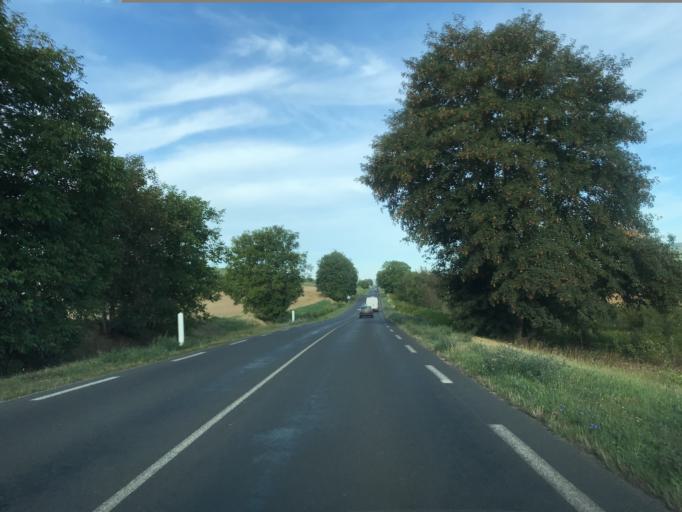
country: FR
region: Champagne-Ardenne
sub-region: Departement de la Marne
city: Mardeuil
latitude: 49.0538
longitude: 3.9025
